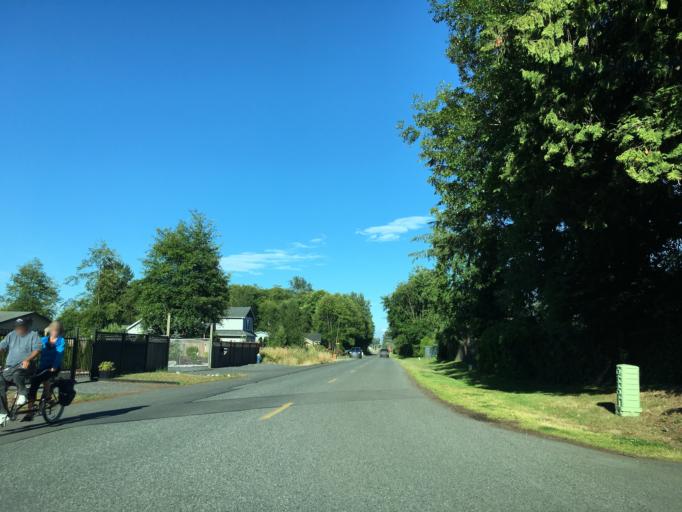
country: US
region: Washington
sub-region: Whatcom County
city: Birch Bay
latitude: 48.9069
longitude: -122.7535
